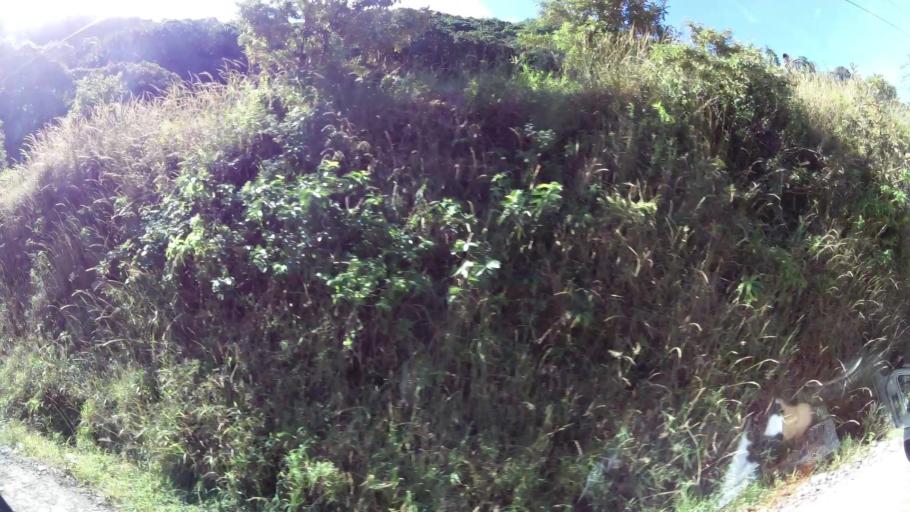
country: CR
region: Guanacaste
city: Juntas
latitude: 10.3311
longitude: -84.8496
